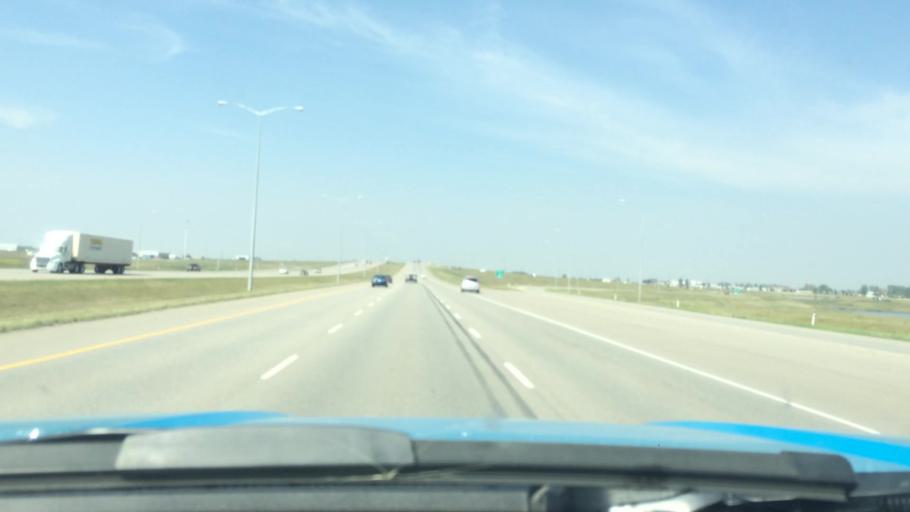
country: CA
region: Alberta
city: Chestermere
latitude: 50.9408
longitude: -113.9201
